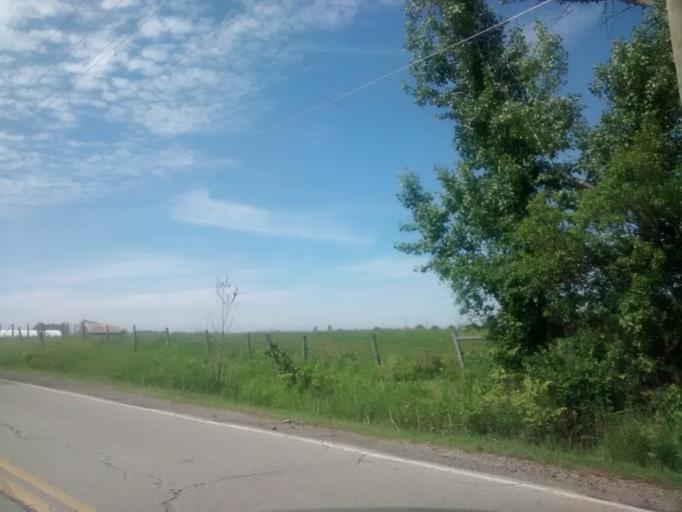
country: CA
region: Ontario
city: Burlington
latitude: 43.4412
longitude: -79.8199
